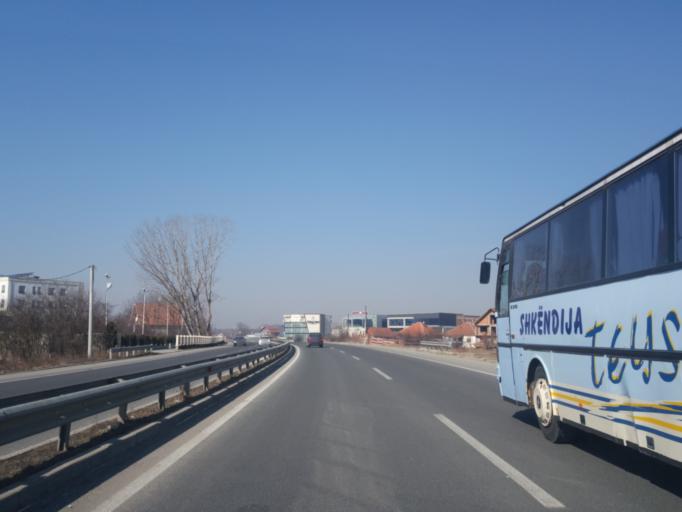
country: XK
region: Pristina
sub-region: Komuna e Obiliqit
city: Obiliq
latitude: 42.7327
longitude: 21.0715
